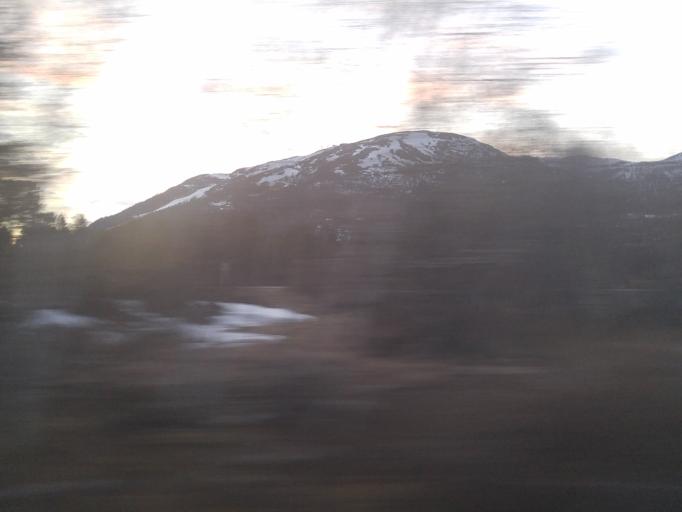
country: NO
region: Sor-Trondelag
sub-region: Oppdal
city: Oppdal
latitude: 62.6002
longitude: 9.7225
